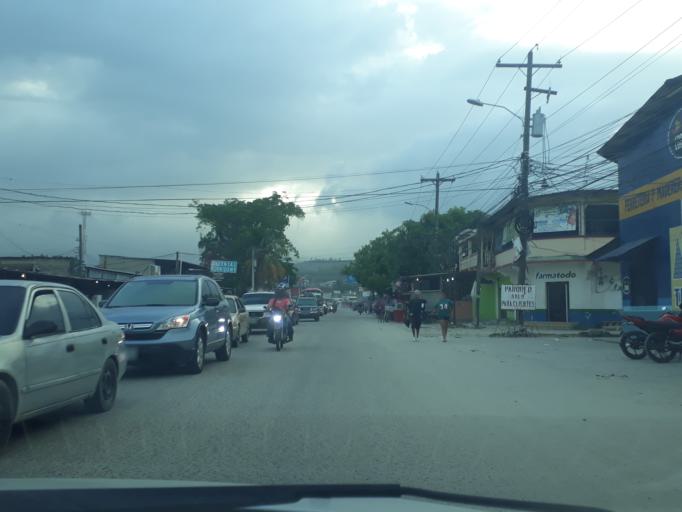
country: HN
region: Cortes
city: Choloma
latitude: 15.5728
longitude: -87.9514
